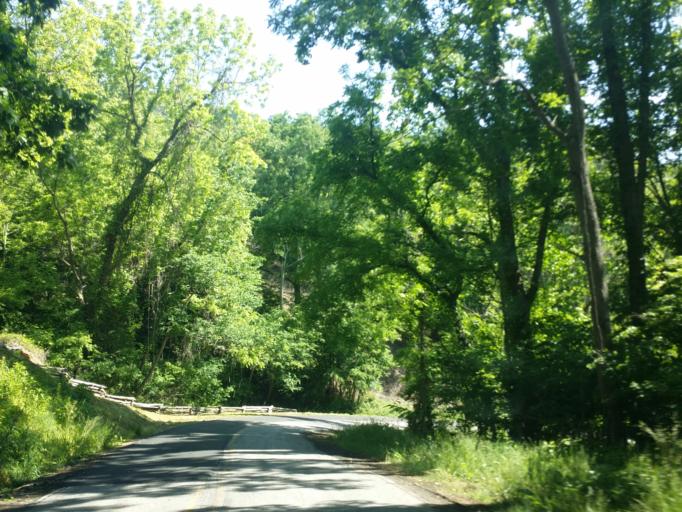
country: US
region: North Carolina
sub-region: Haywood County
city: Cove Creek
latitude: 35.7736
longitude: -82.8909
